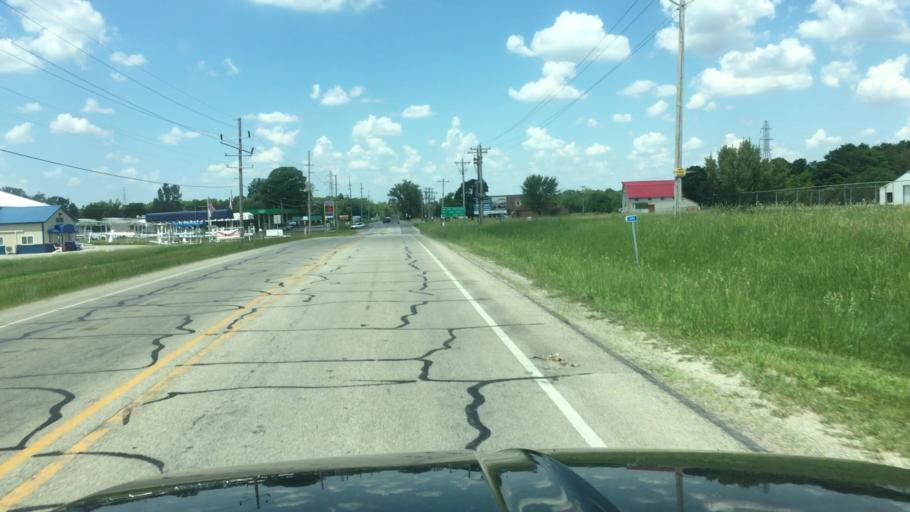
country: US
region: Indiana
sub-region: Kosciusko County
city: North Webster
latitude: 41.3061
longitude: -85.6909
